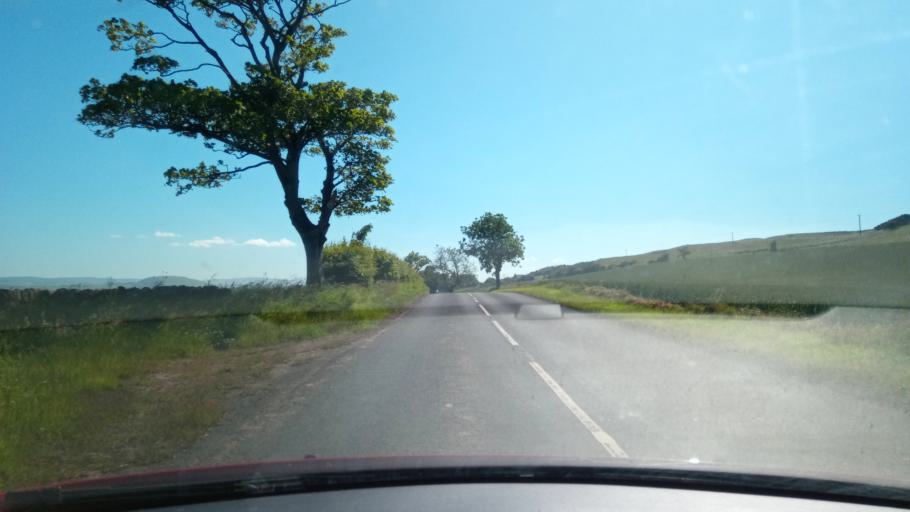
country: GB
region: Scotland
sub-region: East Lothian
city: East Linton
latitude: 56.0309
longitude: -2.6416
